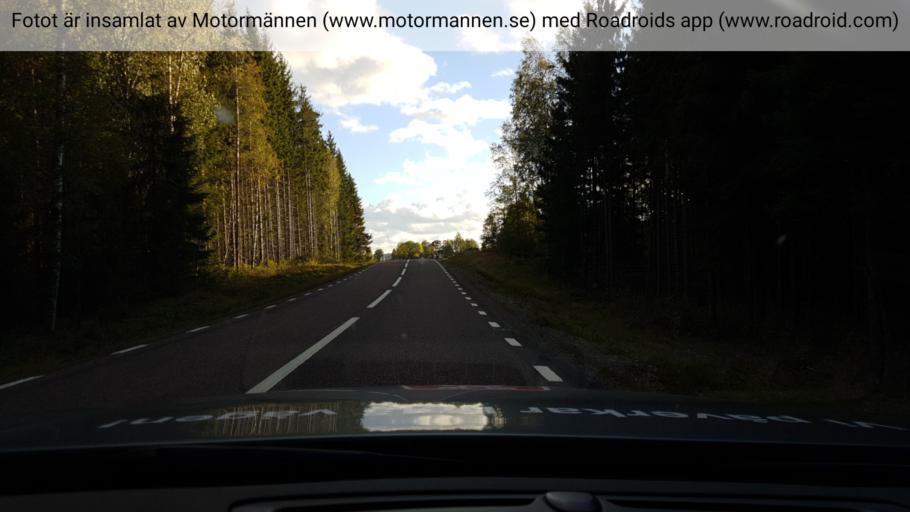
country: SE
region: Vaermland
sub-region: Karlstads Kommun
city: Molkom
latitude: 59.7248
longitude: 13.6786
